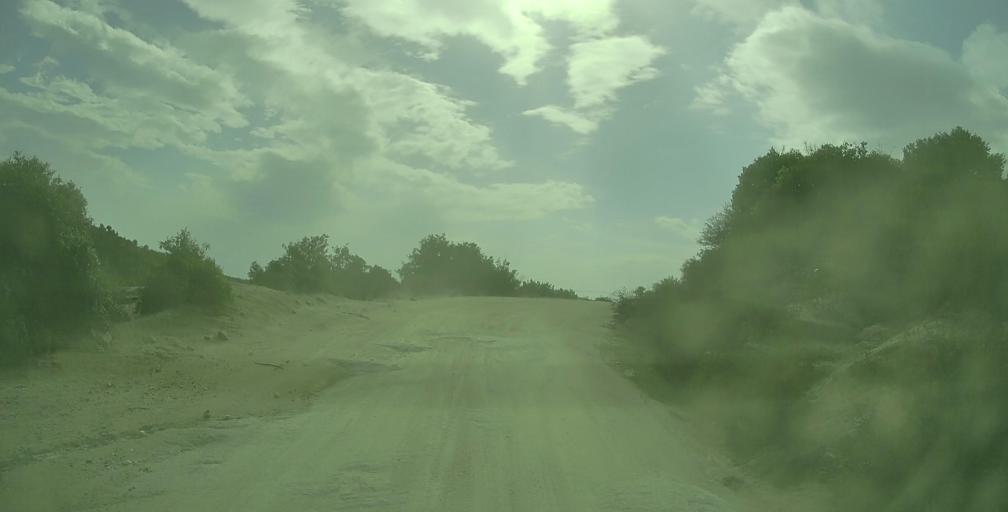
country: GR
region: Central Macedonia
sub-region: Nomos Chalkidikis
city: Sykia
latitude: 40.0007
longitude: 23.9264
